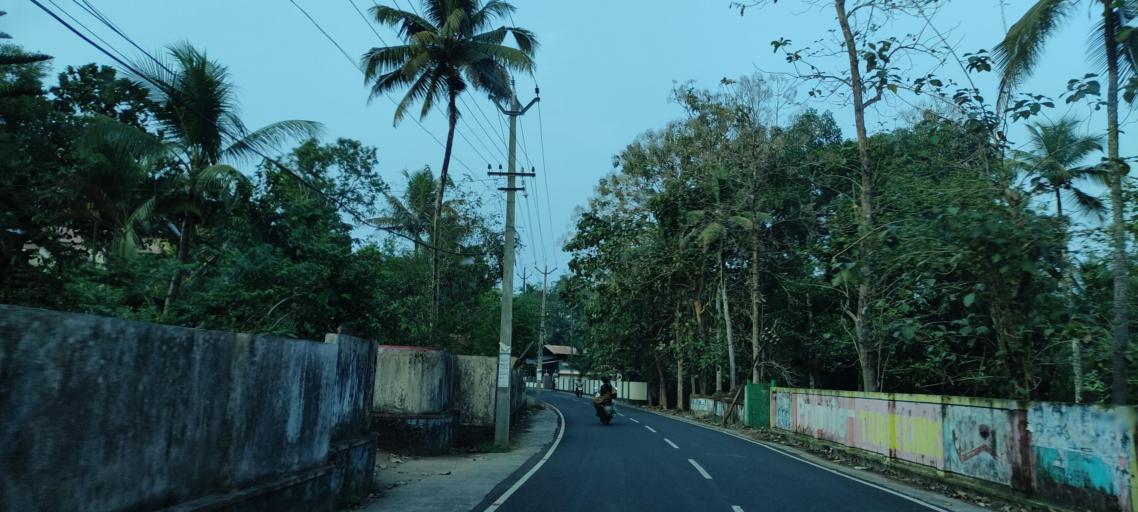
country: IN
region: Kerala
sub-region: Alappuzha
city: Mavelikara
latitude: 9.2678
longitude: 76.5558
